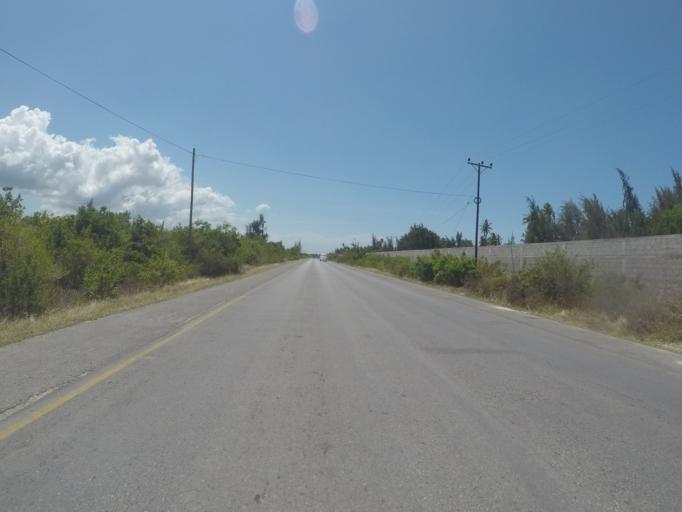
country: TZ
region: Zanzibar Central/South
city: Nganane
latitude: -6.2794
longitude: 39.5348
